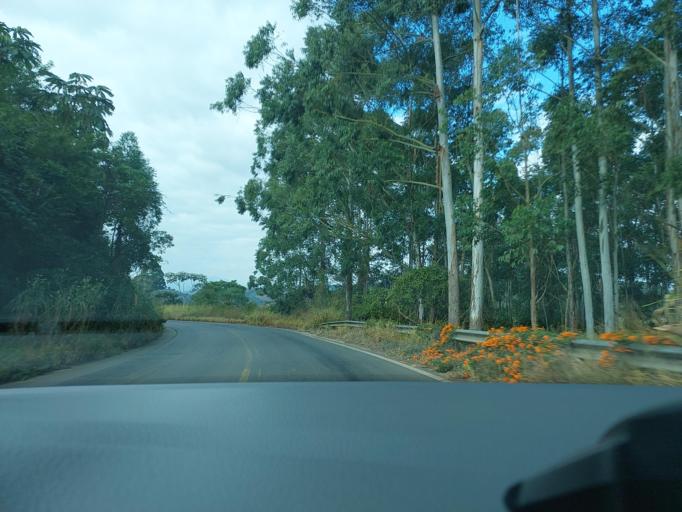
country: BR
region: Minas Gerais
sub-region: Vicosa
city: Vicosa
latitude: -20.8409
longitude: -42.7055
